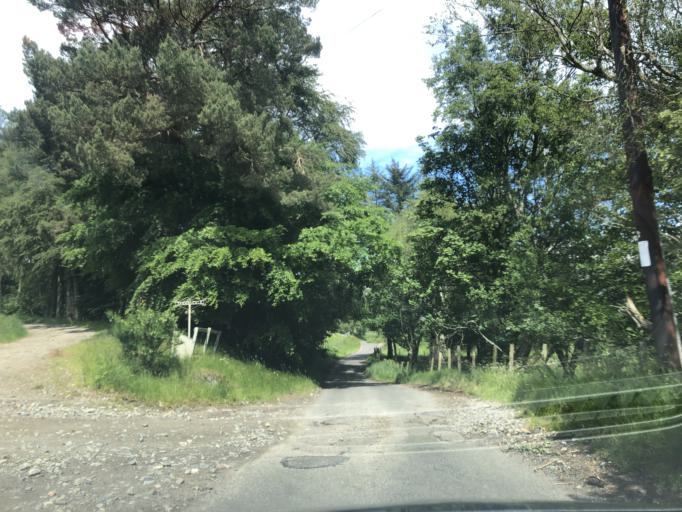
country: GB
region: Scotland
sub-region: Angus
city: Kirriemuir
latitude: 56.7934
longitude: -3.0457
